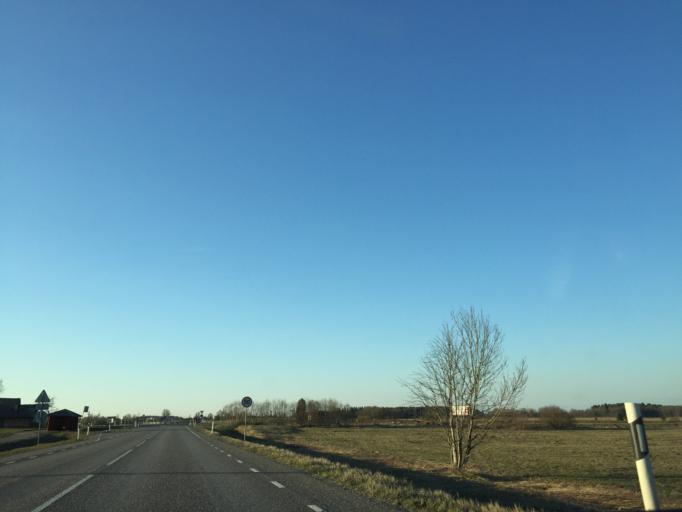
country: EE
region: Ida-Virumaa
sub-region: Johvi vald
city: Johvi
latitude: 59.2929
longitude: 27.4956
